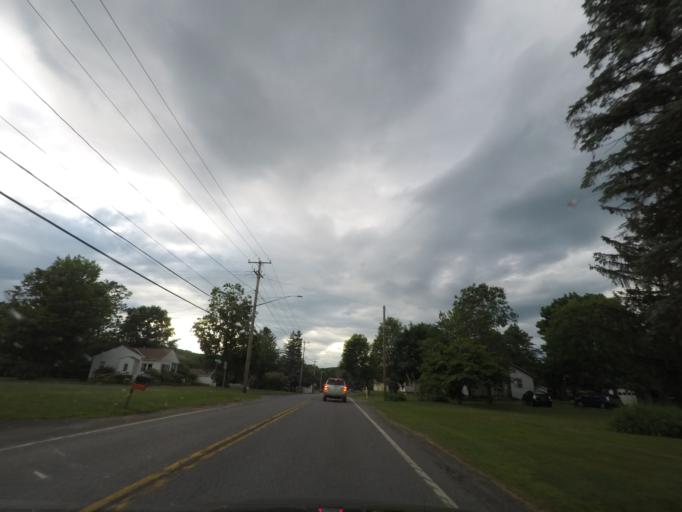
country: US
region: New York
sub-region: Dutchess County
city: Pine Plains
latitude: 41.9822
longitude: -73.6649
